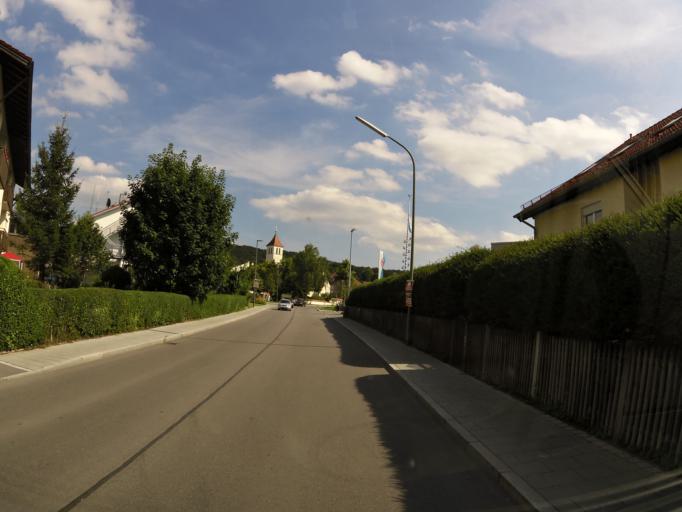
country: DE
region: Bavaria
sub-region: Upper Bavaria
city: Herrsching am Ammersee
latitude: 48.0001
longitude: 11.1738
